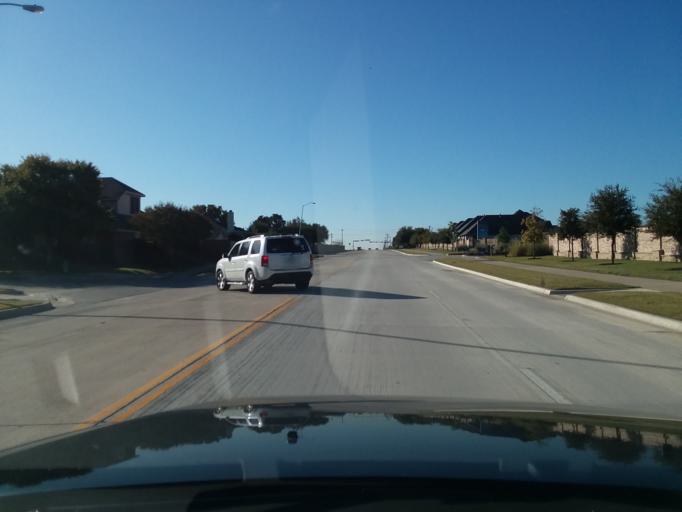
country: US
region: Texas
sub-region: Denton County
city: Lewisville
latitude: 33.0128
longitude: -97.0277
